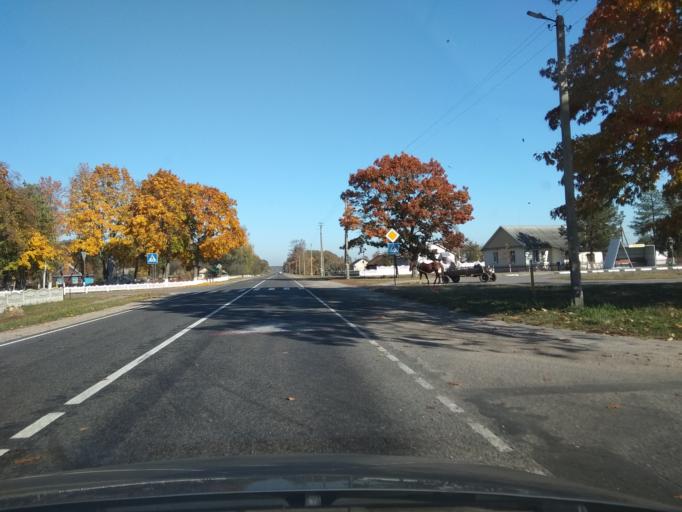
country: BY
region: Brest
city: Malaryta
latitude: 51.9866
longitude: 24.2062
